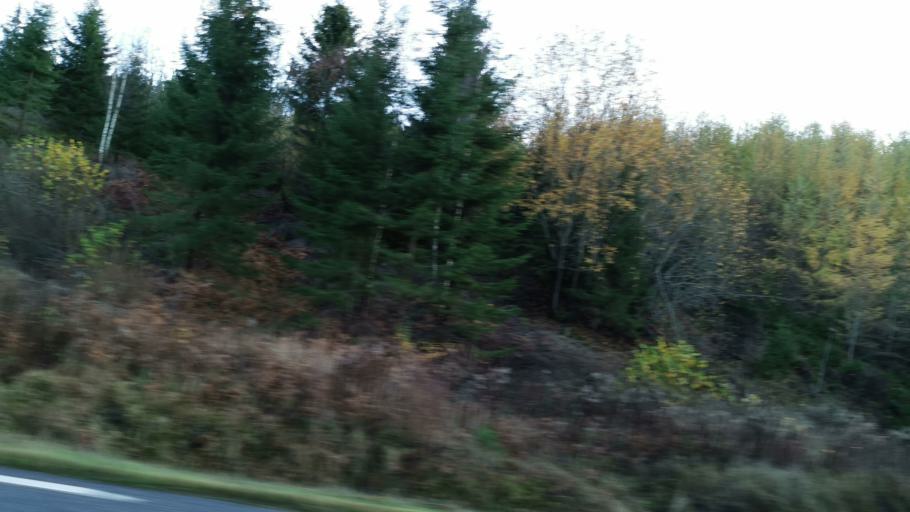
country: SE
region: Vaestra Goetaland
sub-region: Munkedals Kommun
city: Munkedal
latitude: 58.4902
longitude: 11.7167
